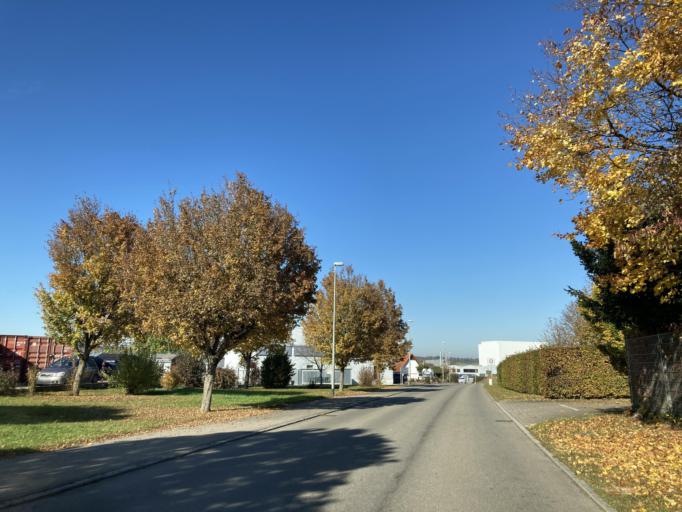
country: DE
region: Baden-Wuerttemberg
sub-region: Tuebingen Region
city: Ofterdingen
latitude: 48.4157
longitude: 9.0396
